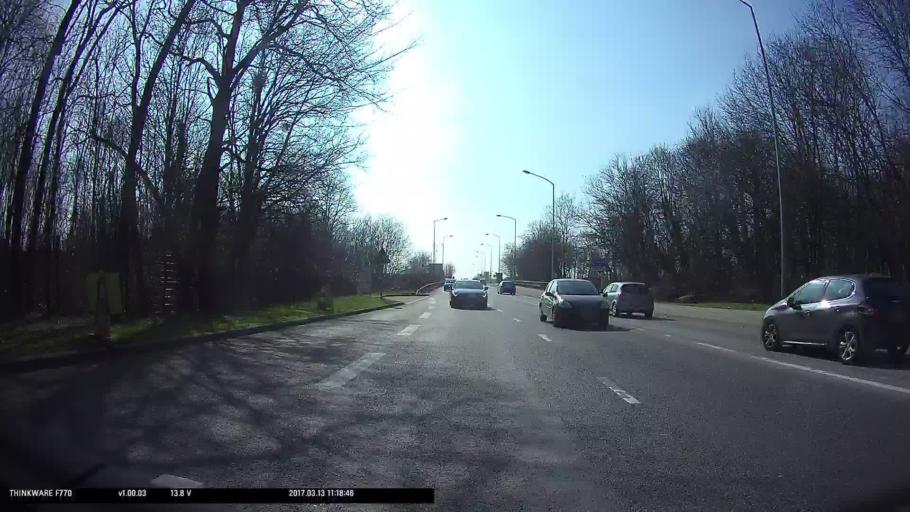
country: FR
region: Ile-de-France
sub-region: Departement de Seine-et-Marne
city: Champs-sur-Marne
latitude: 48.8370
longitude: 2.5824
